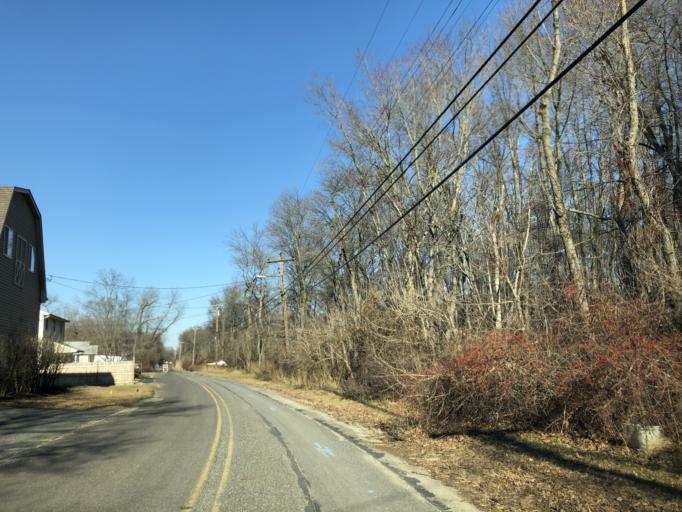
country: US
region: Pennsylvania
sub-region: Delaware County
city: Chester
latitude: 39.8031
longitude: -75.3544
